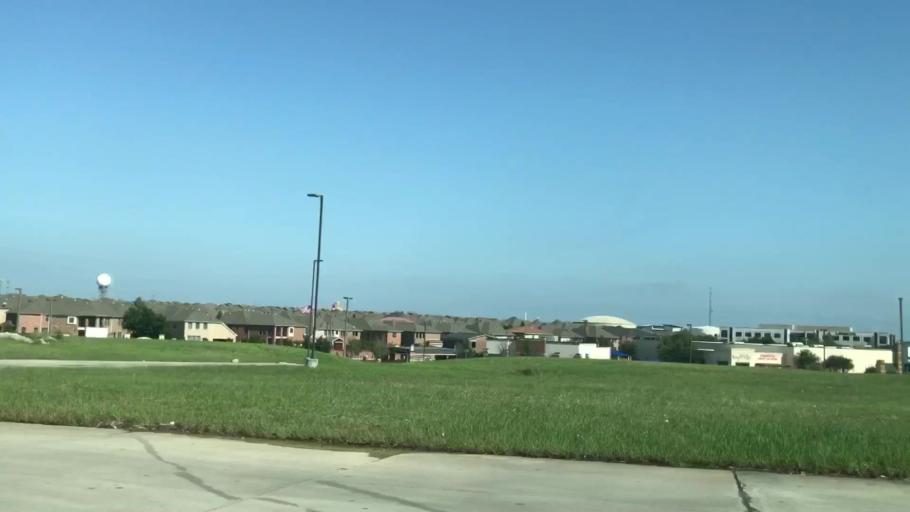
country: US
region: Texas
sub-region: Dallas County
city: Coppell
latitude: 32.9218
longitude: -96.9755
